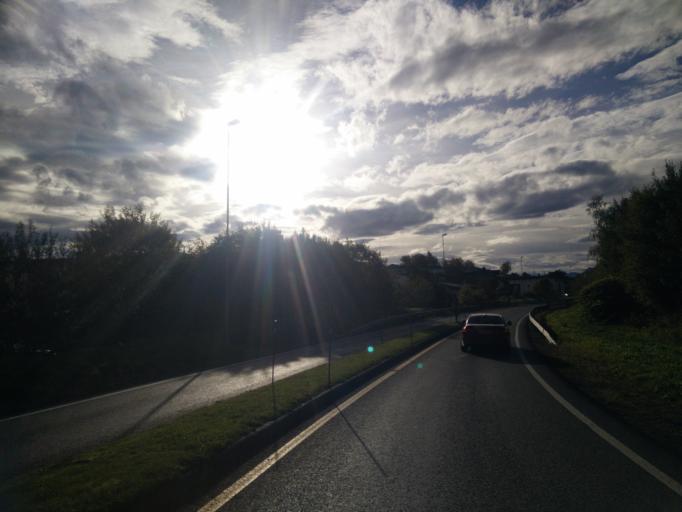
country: NO
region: More og Romsdal
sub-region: Vestnes
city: Vestnes
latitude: 62.6223
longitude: 7.0886
